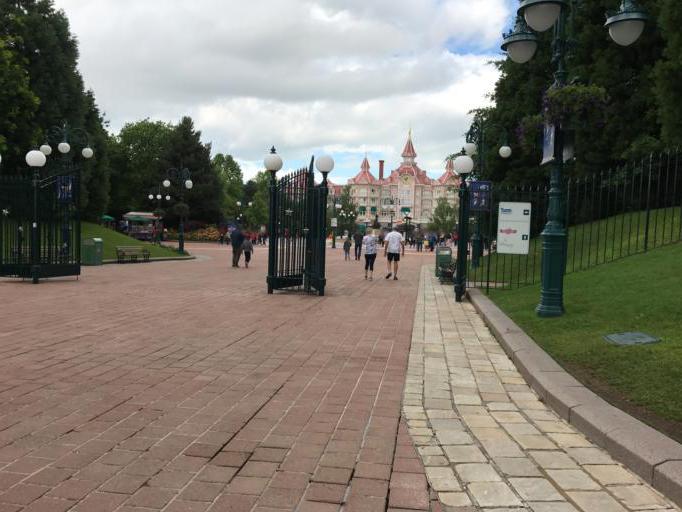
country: FR
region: Ile-de-France
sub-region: Departement de Seine-et-Marne
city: Chessy
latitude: 48.8690
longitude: 2.7816
